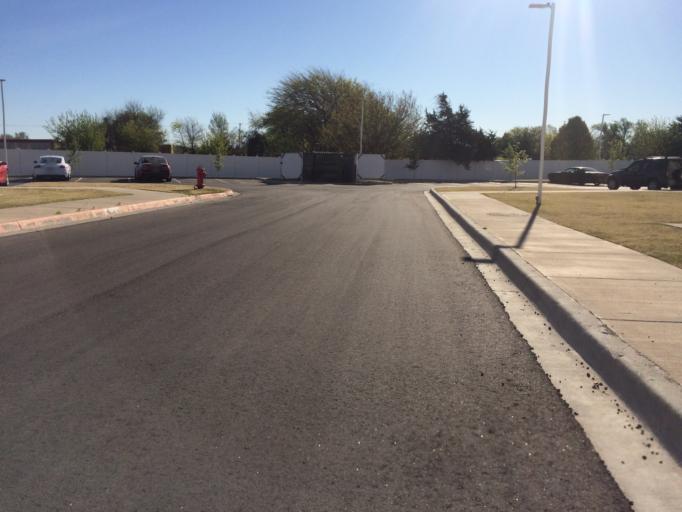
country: US
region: Oklahoma
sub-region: Cleveland County
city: Noble
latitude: 35.1776
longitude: -97.4171
